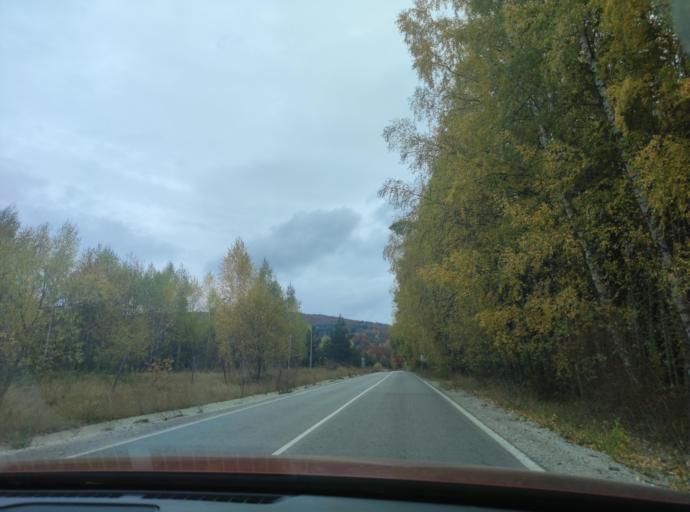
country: BG
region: Sofiya
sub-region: Obshtina Godech
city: Godech
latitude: 43.1012
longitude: 23.1018
